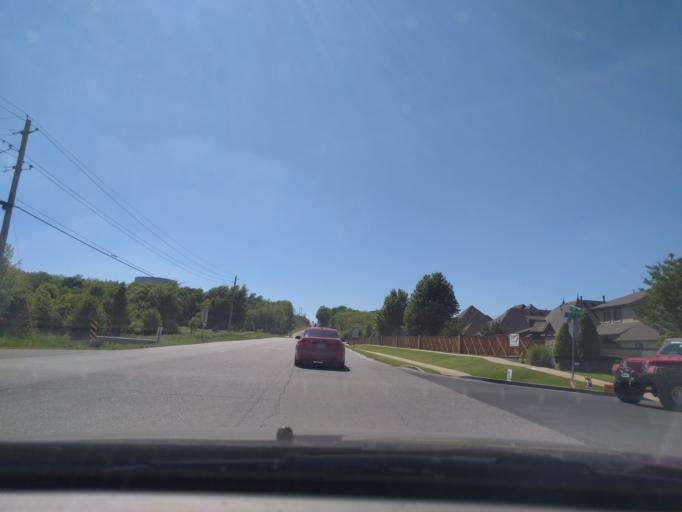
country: US
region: Oklahoma
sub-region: Tulsa County
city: Broken Arrow
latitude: 36.0900
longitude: -95.7927
